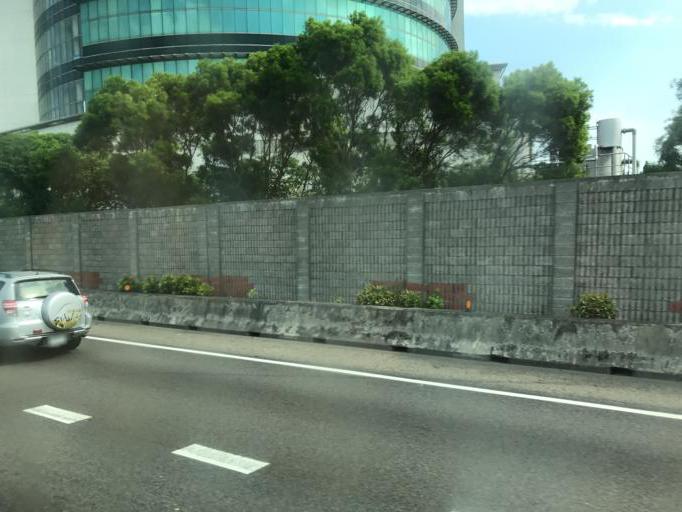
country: TW
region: Taiwan
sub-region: Hsinchu
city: Zhubei
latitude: 24.8717
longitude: 121.0197
